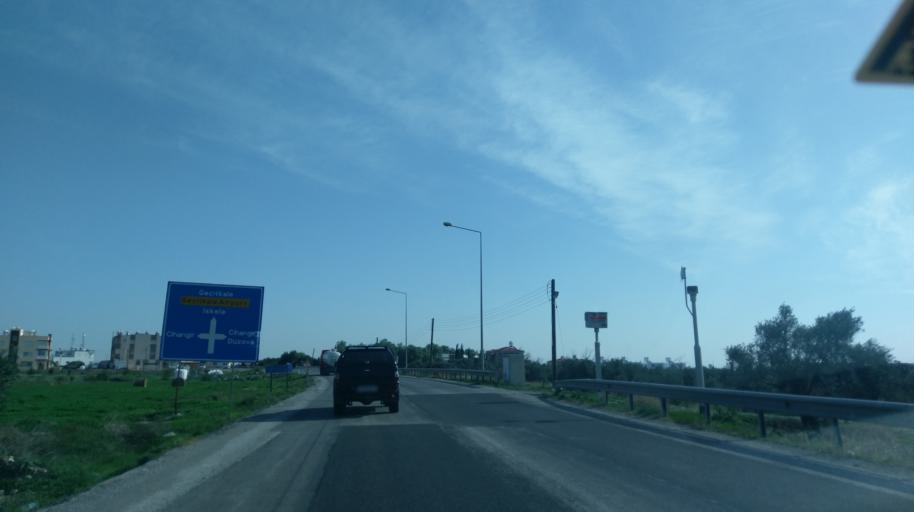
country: CY
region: Lefkosia
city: Geri
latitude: 35.2216
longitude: 33.5129
